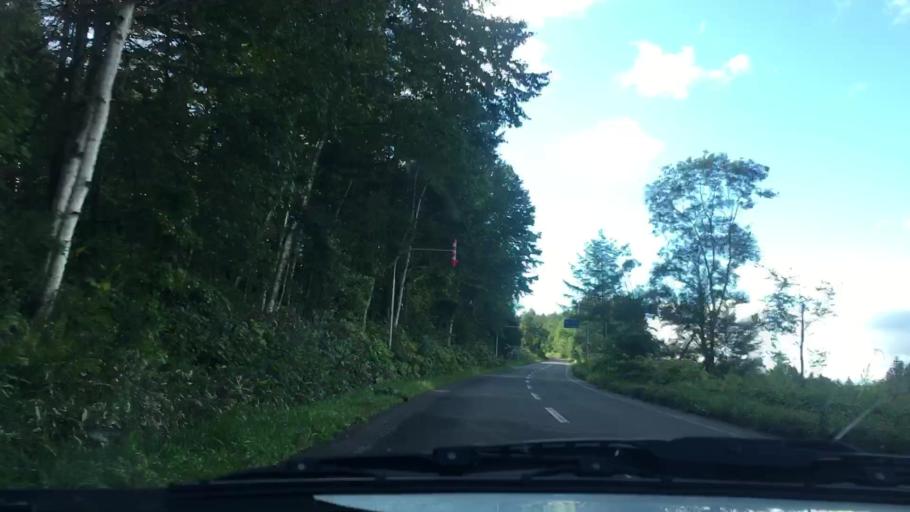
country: JP
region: Hokkaido
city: Otofuke
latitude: 43.1707
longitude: 142.9777
